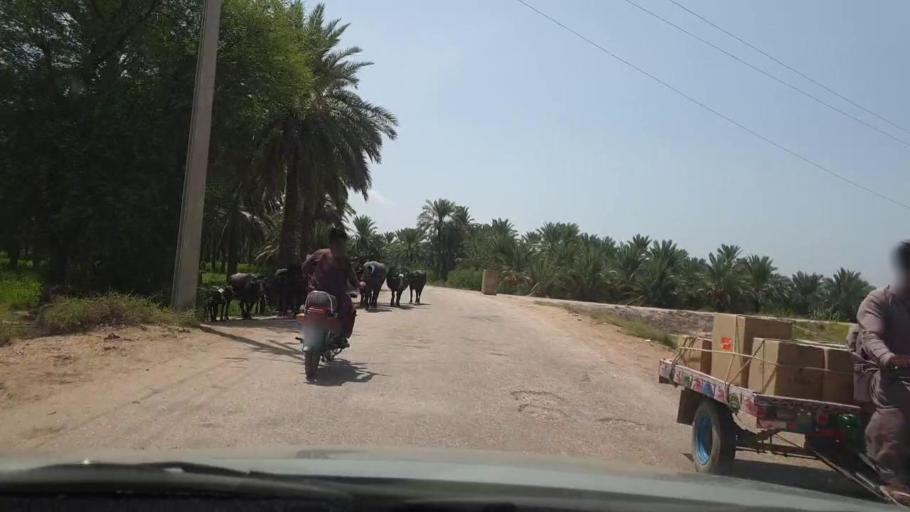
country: PK
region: Sindh
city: Pano Aqil
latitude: 27.6696
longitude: 69.0855
